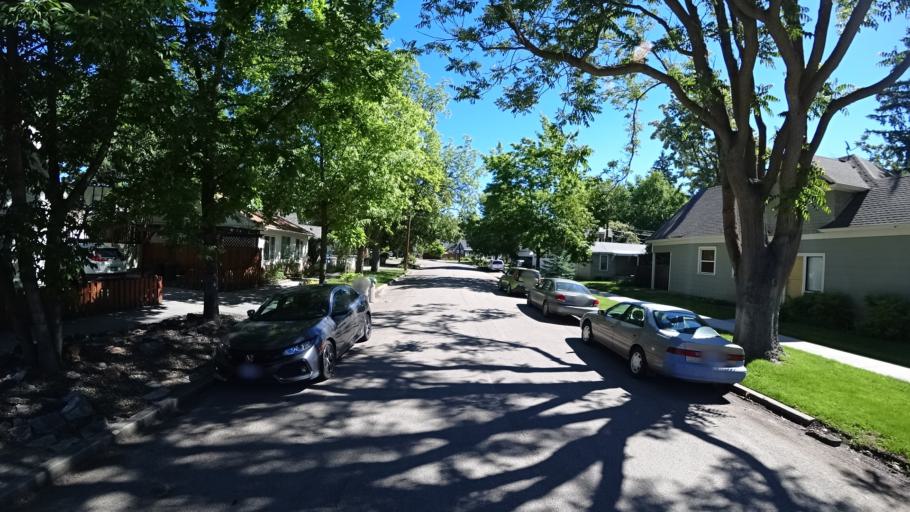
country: US
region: Idaho
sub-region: Ada County
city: Boise
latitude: 43.6261
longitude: -116.2127
